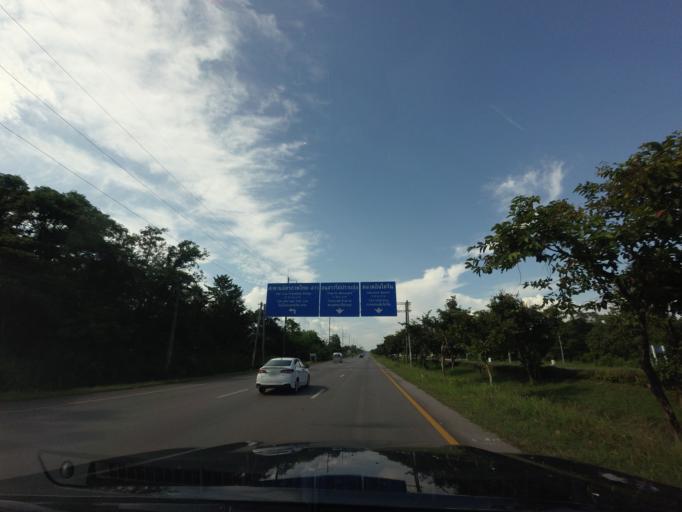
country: TH
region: Nong Khai
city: Nong Khai
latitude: 17.7859
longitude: 102.7645
